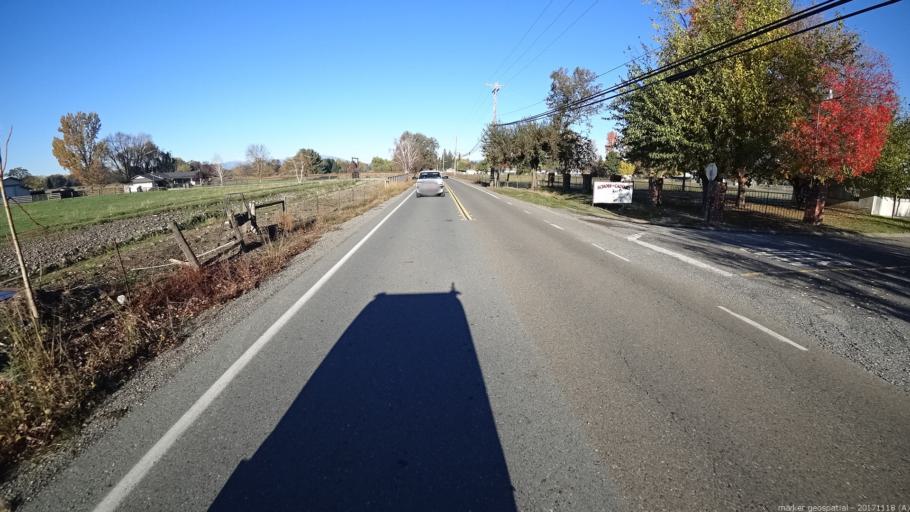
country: US
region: California
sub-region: Shasta County
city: Anderson
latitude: 40.4519
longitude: -122.2690
